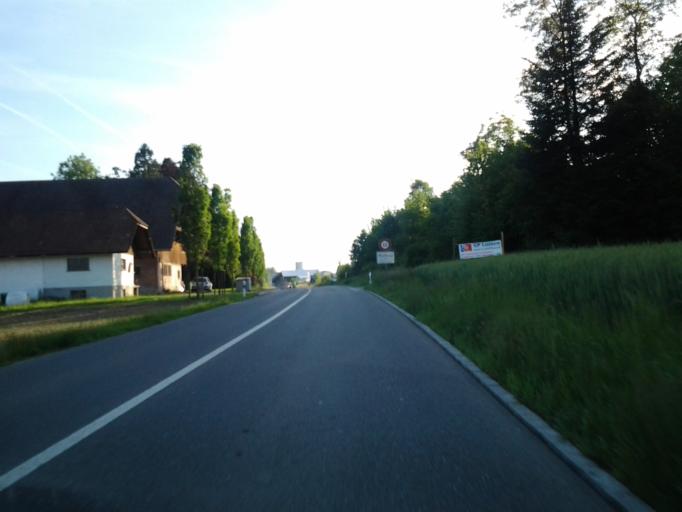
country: CH
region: Lucerne
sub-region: Willisau District
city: Pfaffnau
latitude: 47.2357
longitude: 7.9125
